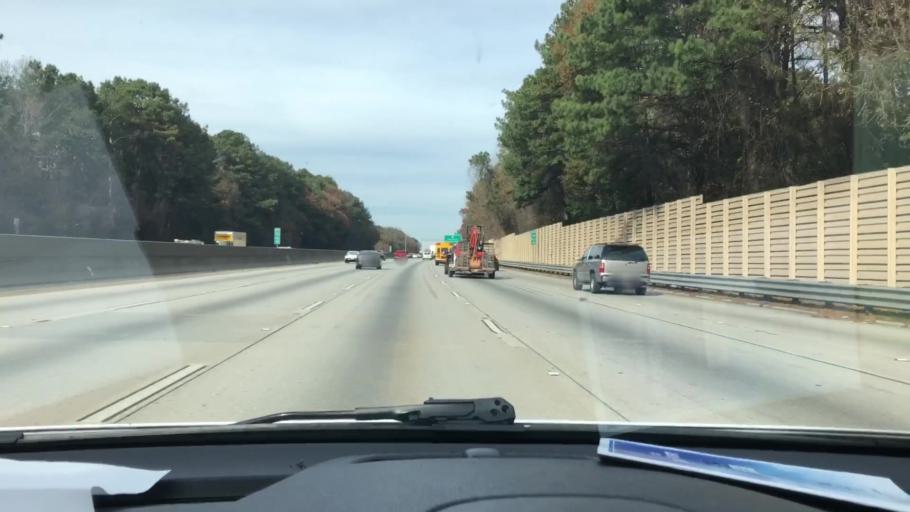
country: US
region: Georgia
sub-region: DeKalb County
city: Belvedere Park
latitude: 33.7563
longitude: -84.2322
